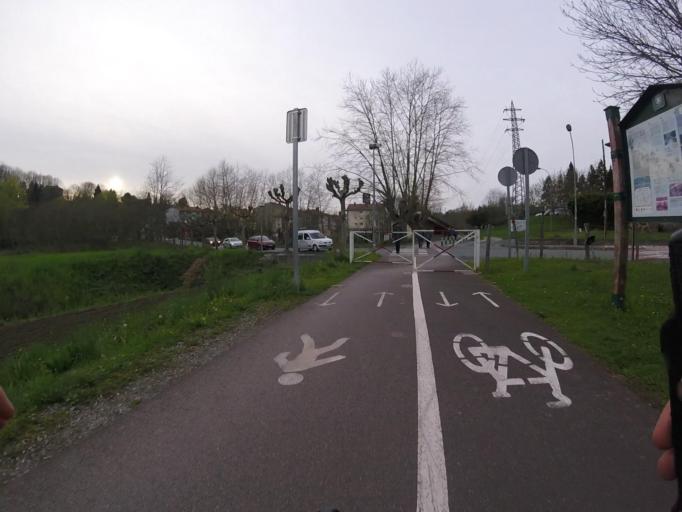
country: ES
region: Basque Country
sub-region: Provincia de Guipuzcoa
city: Errenteria
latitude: 43.2985
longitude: -1.8748
